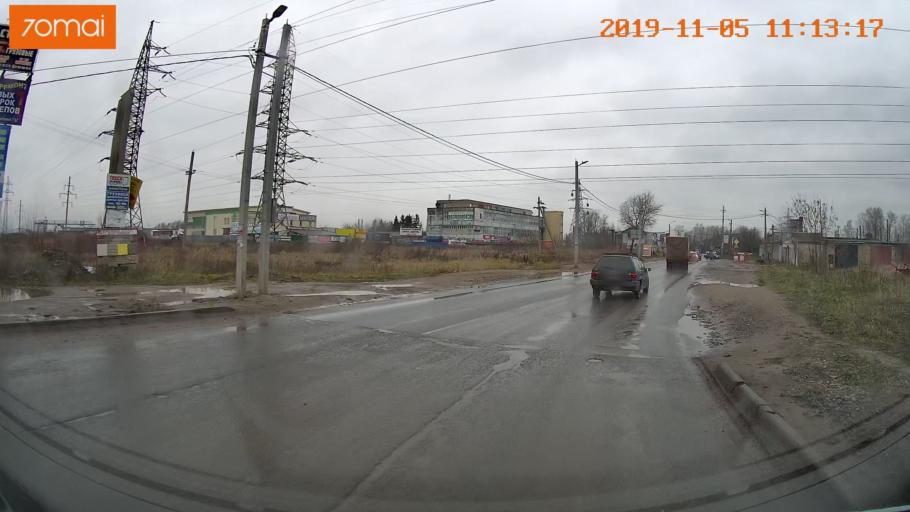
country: RU
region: Ivanovo
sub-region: Gorod Ivanovo
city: Ivanovo
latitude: 56.9660
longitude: 40.9523
